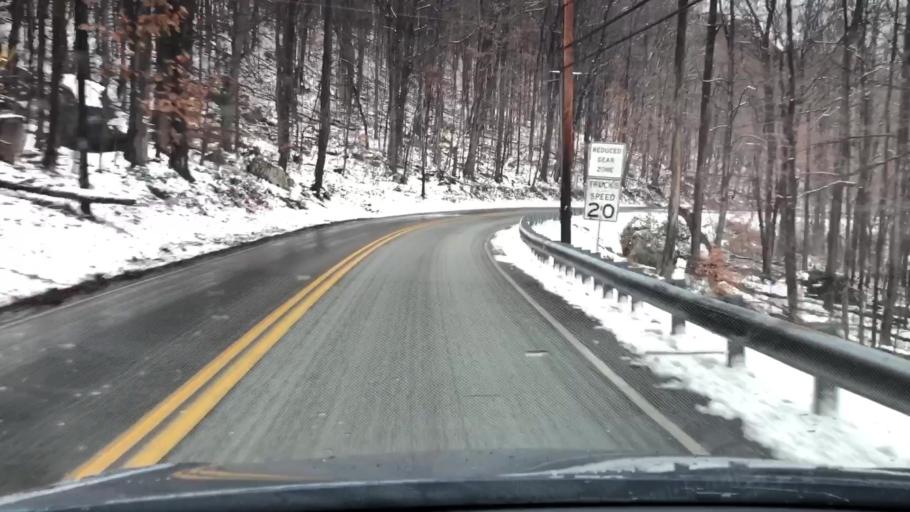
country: US
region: Pennsylvania
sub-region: Fayette County
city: South Connellsville
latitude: 39.8577
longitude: -79.4984
